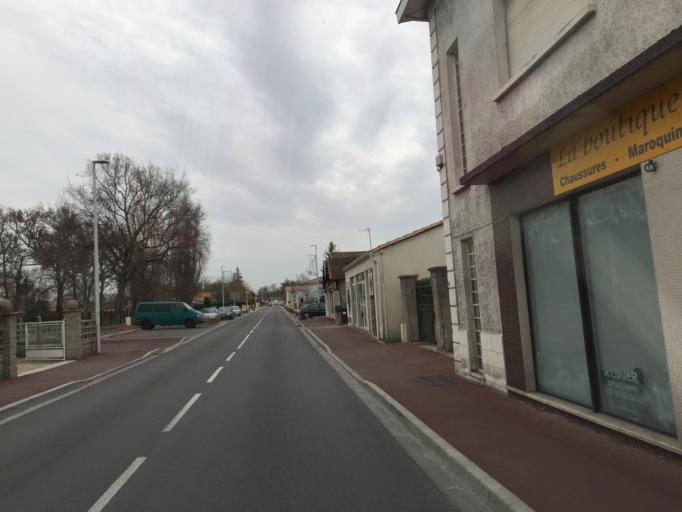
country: FR
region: Aquitaine
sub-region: Departement de la Gironde
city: Carcans
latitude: 45.0779
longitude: -1.0460
